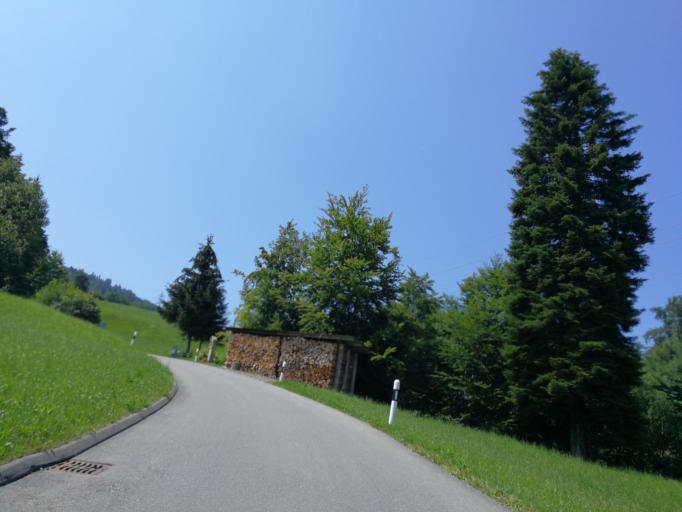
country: CH
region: Schwyz
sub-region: Bezirk March
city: Altendorf
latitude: 47.1862
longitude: 8.7999
